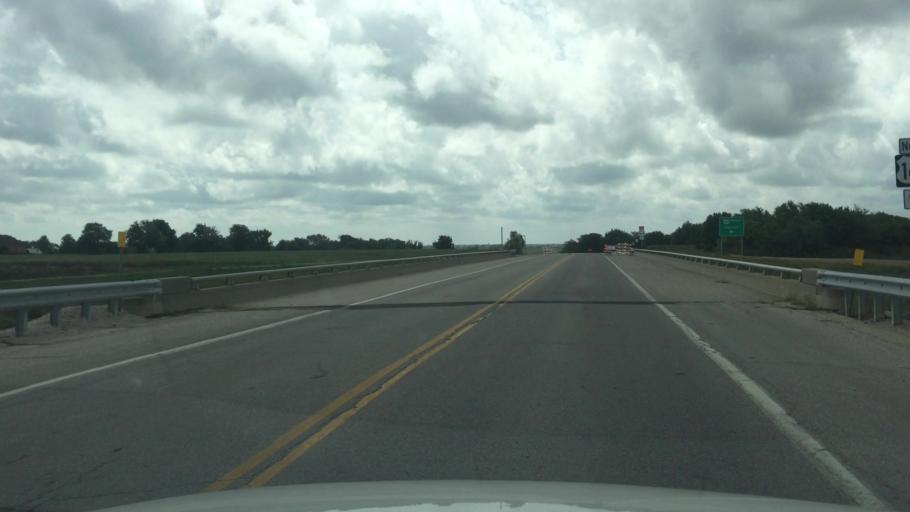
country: US
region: Kansas
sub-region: Allen County
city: Iola
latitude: 37.8809
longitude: -95.3968
